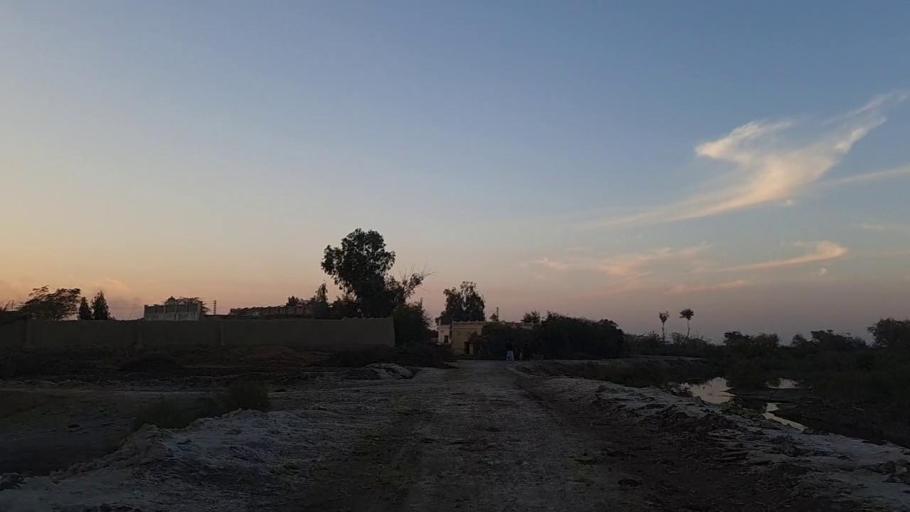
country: PK
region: Sindh
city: Bandhi
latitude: 26.5984
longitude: 68.3377
